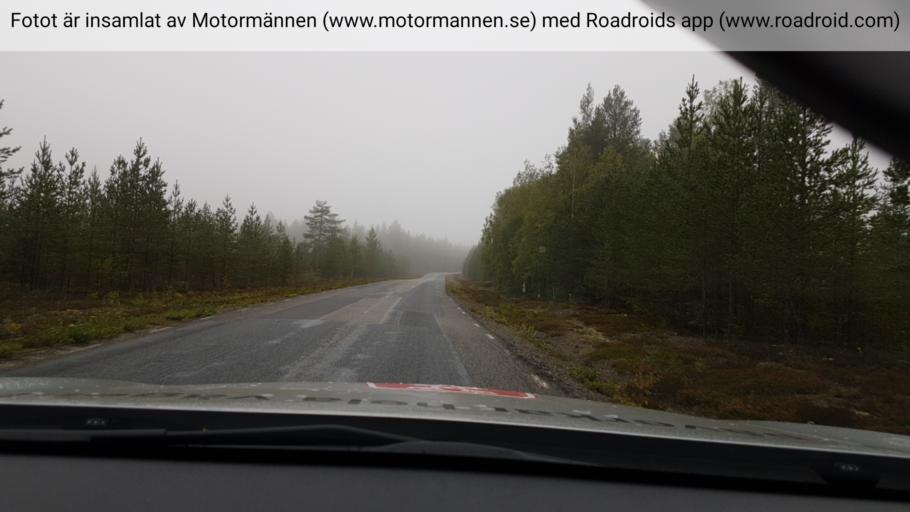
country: SE
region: Vaesterbotten
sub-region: Umea Kommun
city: Ersmark
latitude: 64.2248
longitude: 20.2904
